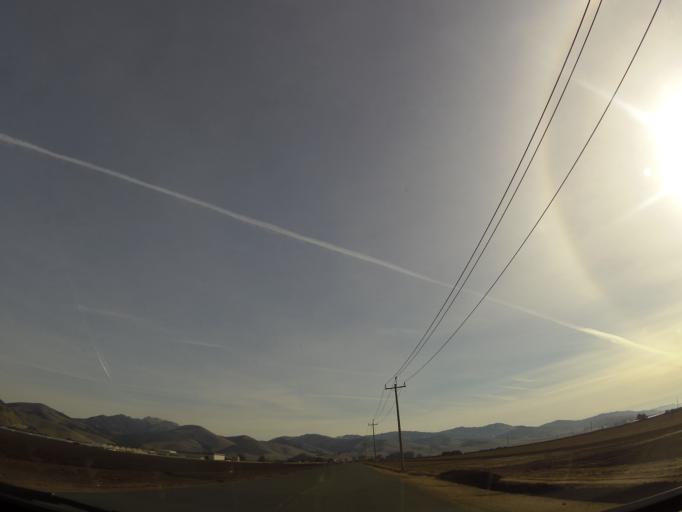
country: US
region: California
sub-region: Monterey County
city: Boronda
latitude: 36.7289
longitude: -121.6232
